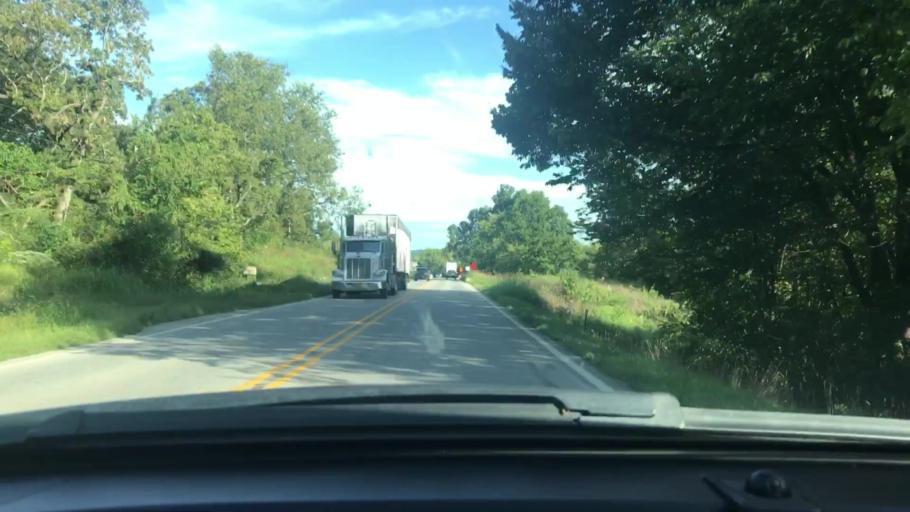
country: US
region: Arkansas
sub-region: Sharp County
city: Cherokee Village
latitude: 36.3062
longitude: -91.4529
